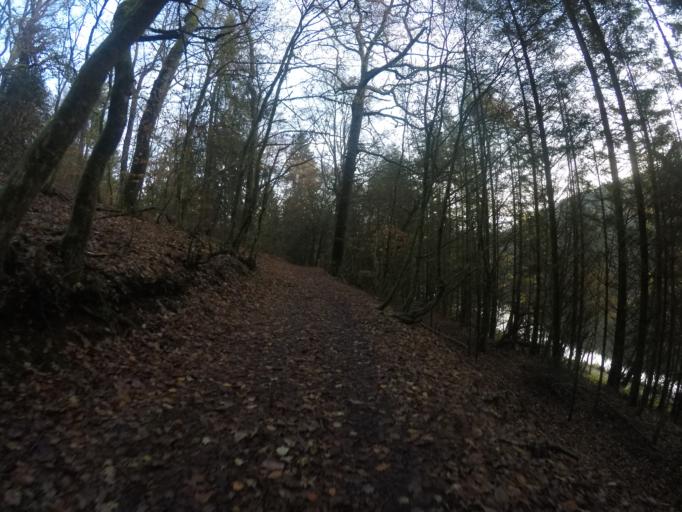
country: BE
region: Wallonia
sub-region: Province du Luxembourg
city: Habay-la-Vieille
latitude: 49.7412
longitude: 5.6720
